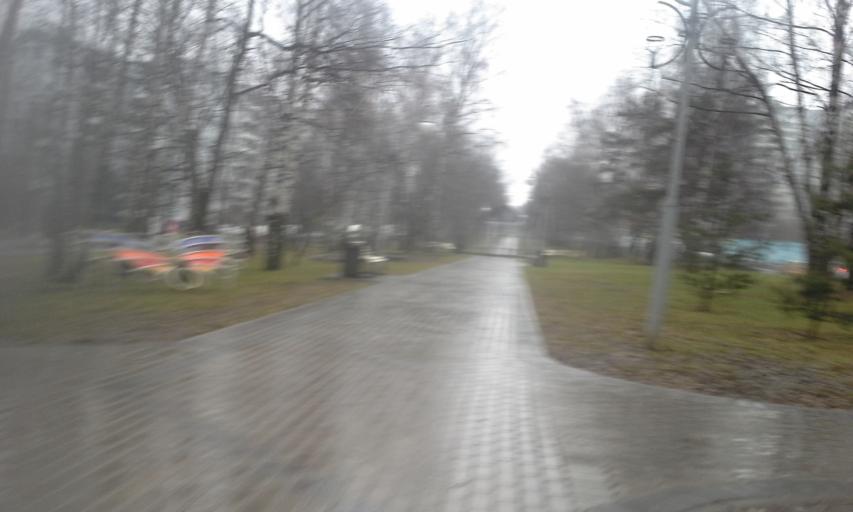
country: RU
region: Moscow
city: Yasenevo
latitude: 55.5903
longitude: 37.5463
